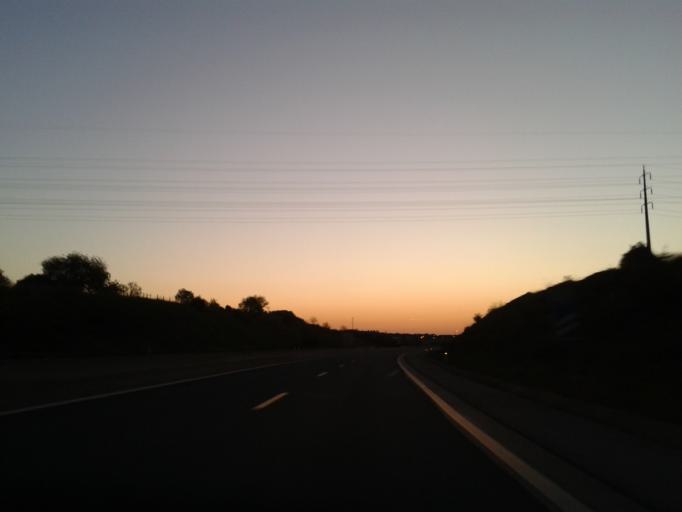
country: PT
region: Faro
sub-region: Albufeira
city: Ferreiras
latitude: 37.1390
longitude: -8.2651
